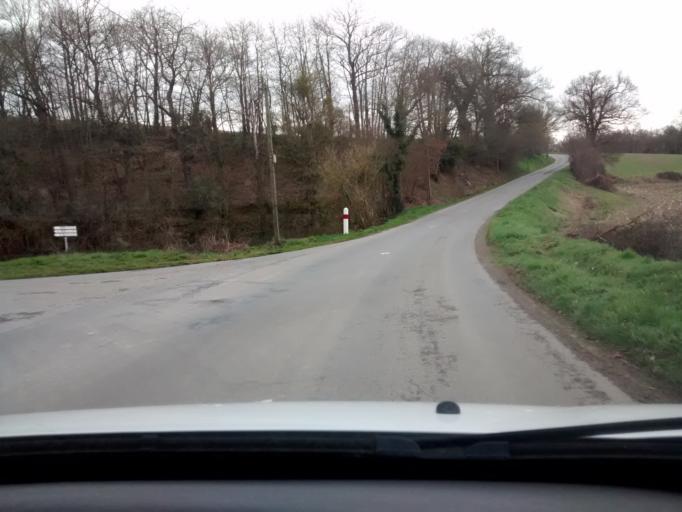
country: FR
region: Brittany
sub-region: Departement d'Ille-et-Vilaine
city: La Bouexiere
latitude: 48.1968
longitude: -1.4649
